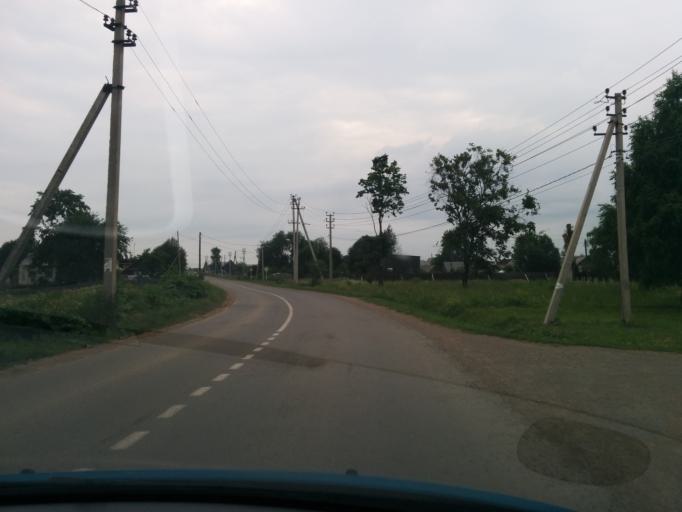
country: RU
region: Perm
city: Polazna
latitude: 58.2324
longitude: 56.2884
